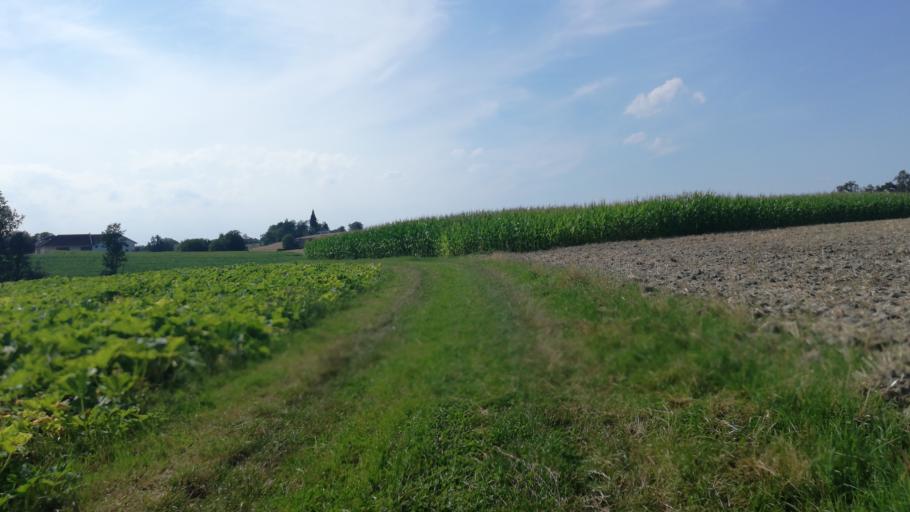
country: AT
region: Upper Austria
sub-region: Wels-Land
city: Gunskirchen
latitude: 48.1704
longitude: 13.9220
